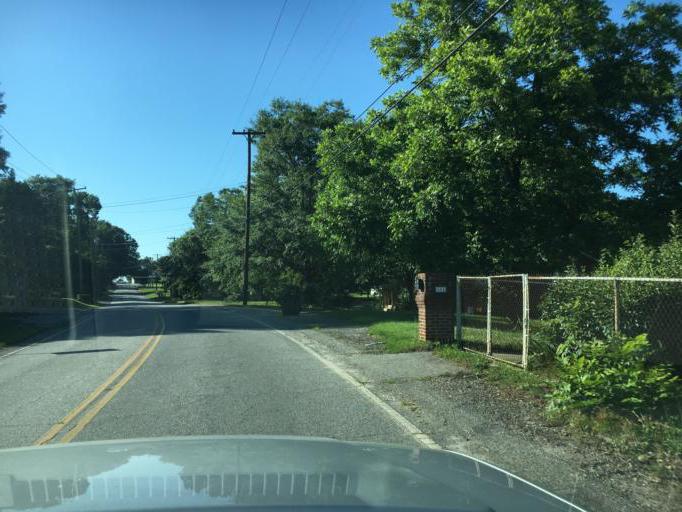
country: US
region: South Carolina
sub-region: Greenville County
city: Greer
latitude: 34.9422
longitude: -82.2157
